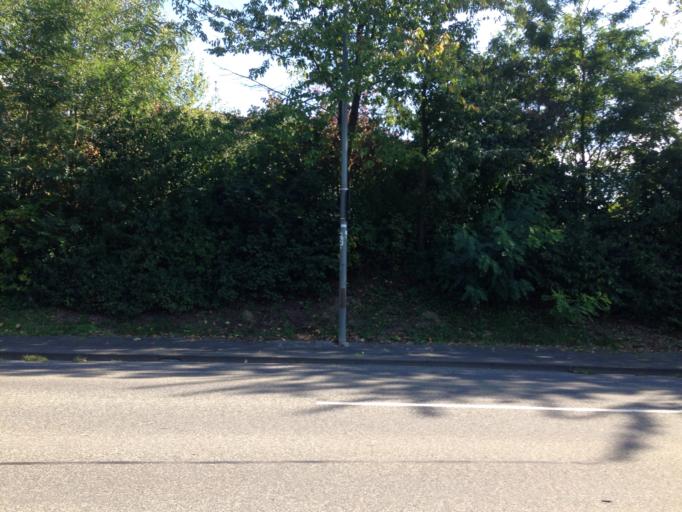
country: DE
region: Hesse
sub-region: Regierungsbezirk Giessen
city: Giessen
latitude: 50.6051
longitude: 8.6734
